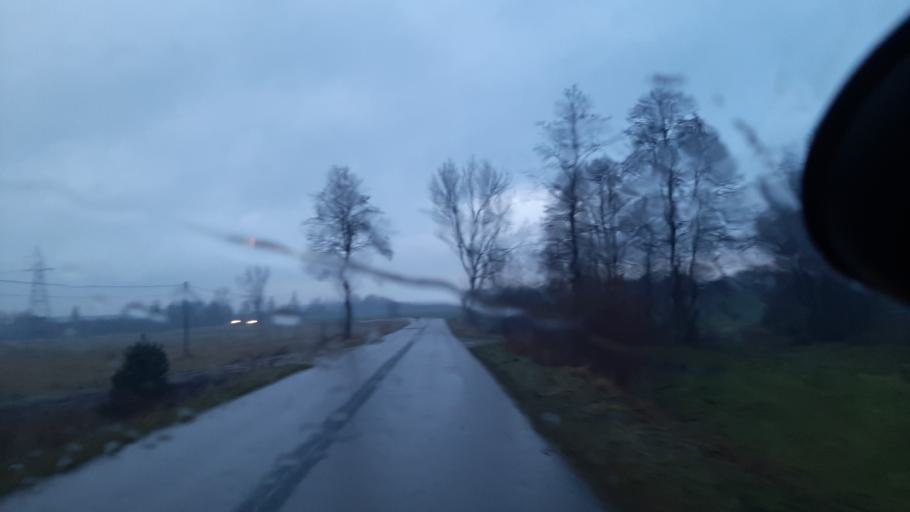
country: PL
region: Lublin Voivodeship
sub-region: Powiat lubartowski
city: Firlej
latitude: 51.5515
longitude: 22.5523
